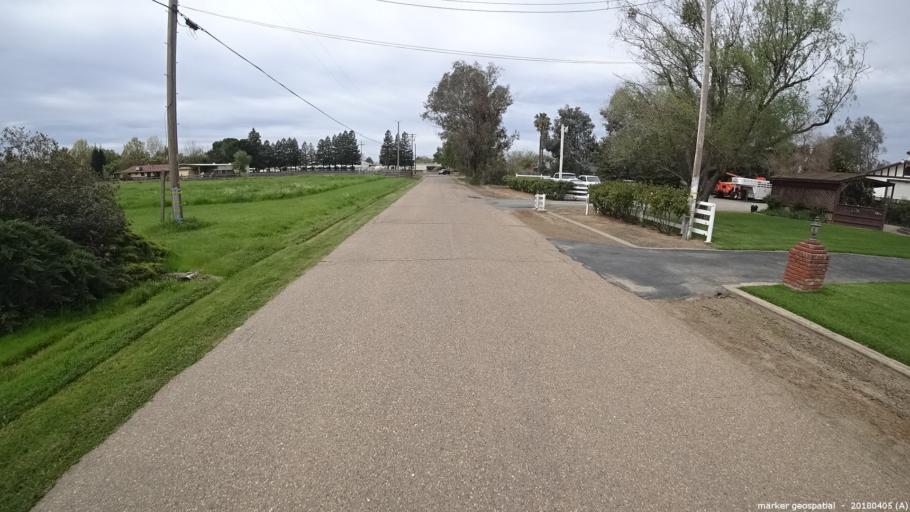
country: US
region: California
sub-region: Sacramento County
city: Galt
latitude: 38.2892
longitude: -121.3243
